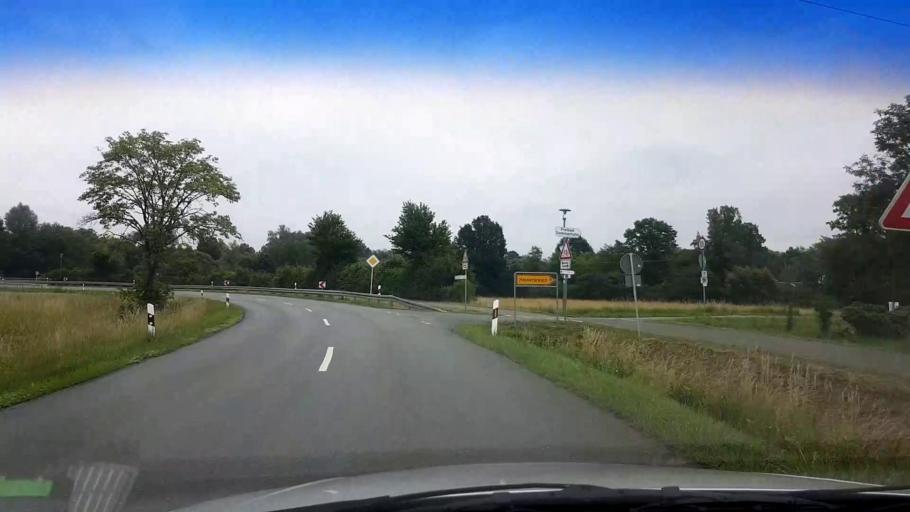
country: DE
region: Bavaria
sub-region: Upper Franconia
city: Mainleus
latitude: 50.0971
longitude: 11.3697
